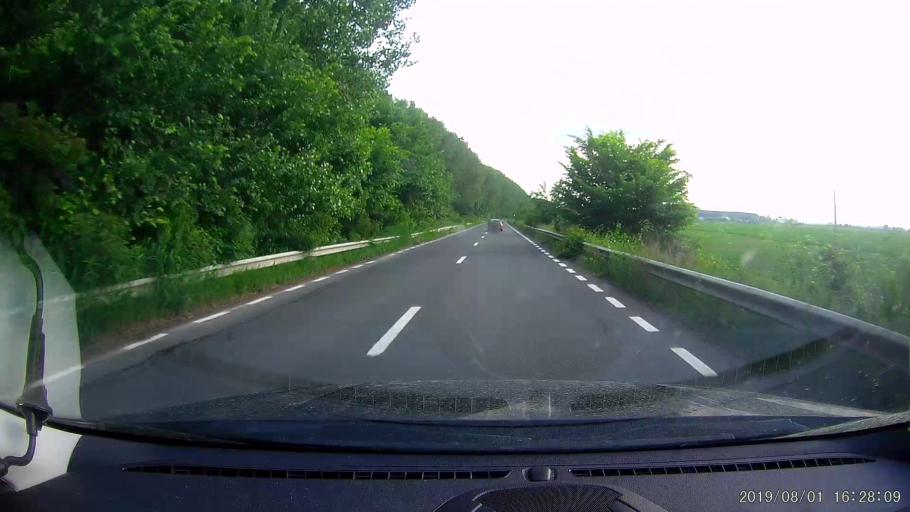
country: RO
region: Calarasi
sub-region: Municipiul Calarasi
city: Calarasi
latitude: 44.1523
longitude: 27.3130
